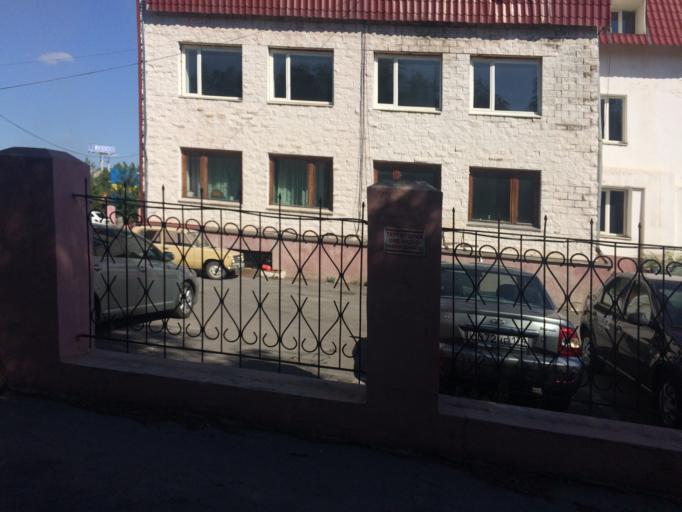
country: RU
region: Chelyabinsk
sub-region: Gorod Magnitogorsk
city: Magnitogorsk
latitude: 53.3969
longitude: 58.9740
